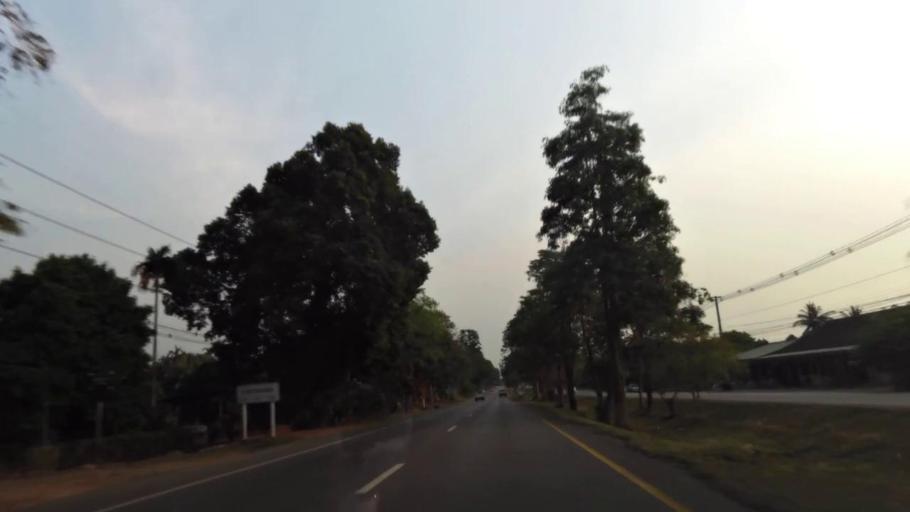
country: TH
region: Chanthaburi
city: Khlung
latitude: 12.4930
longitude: 102.1733
